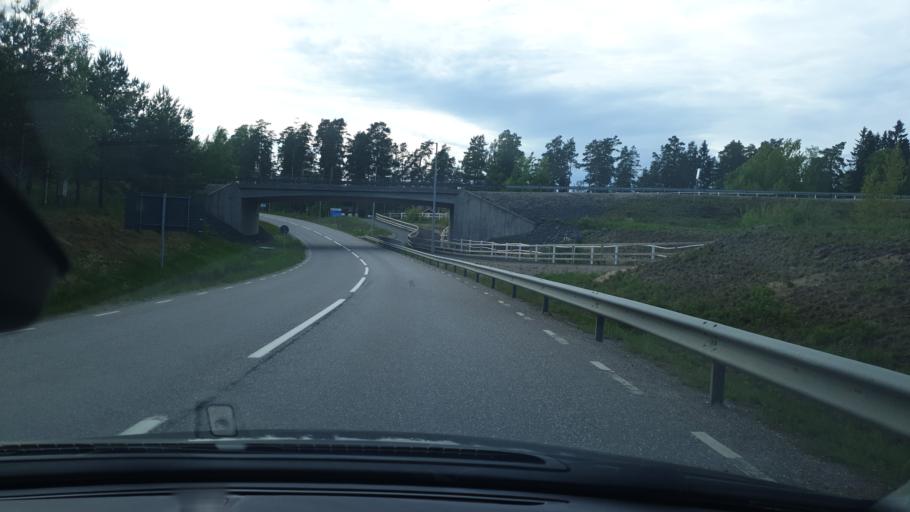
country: SE
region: Joenkoeping
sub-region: Vetlanda Kommun
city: Vetlanda
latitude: 57.4191
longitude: 15.1123
